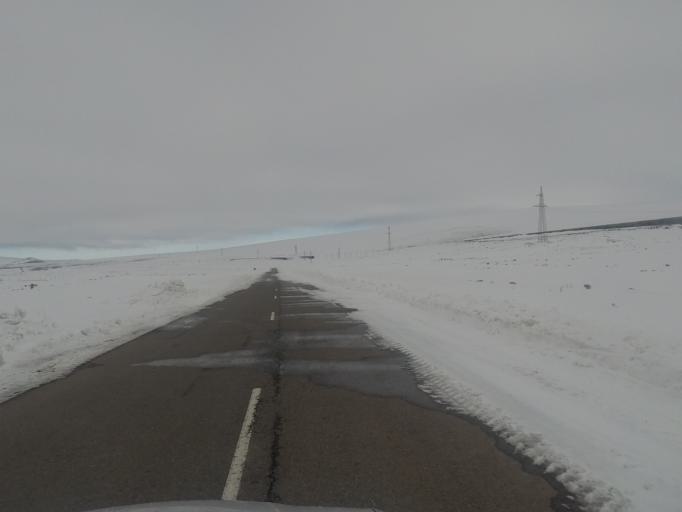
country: GE
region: Samtskhe-Javakheti
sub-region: Ninotsminda
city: Ninotsminda
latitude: 41.4082
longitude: 43.8215
